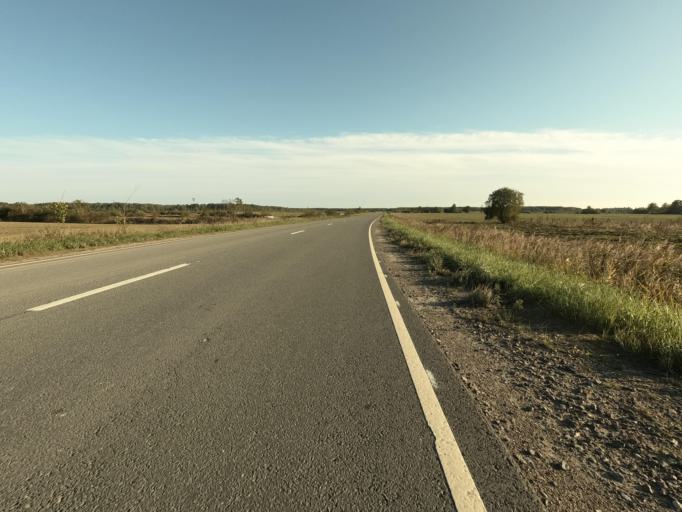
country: RU
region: St.-Petersburg
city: Sapernyy
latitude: 59.7423
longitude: 30.6494
